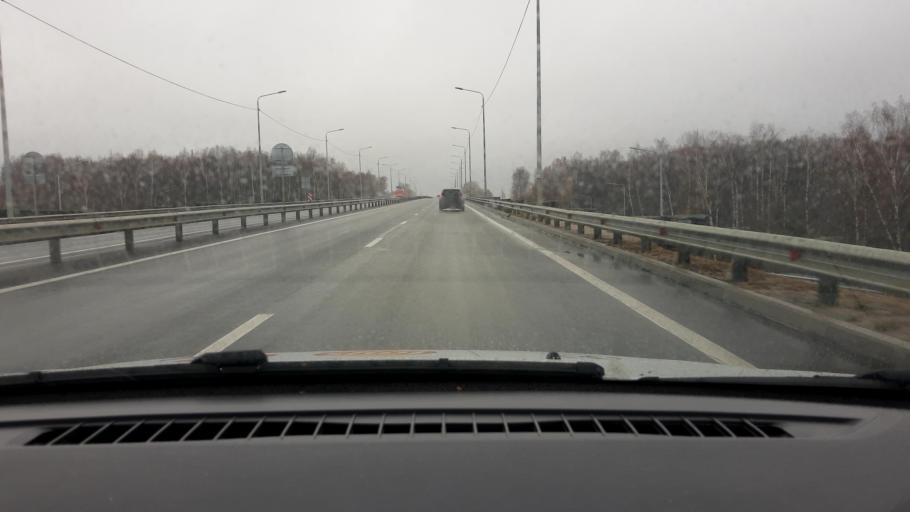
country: RU
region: Nizjnij Novgorod
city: Burevestnik
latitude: 56.0061
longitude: 43.9667
